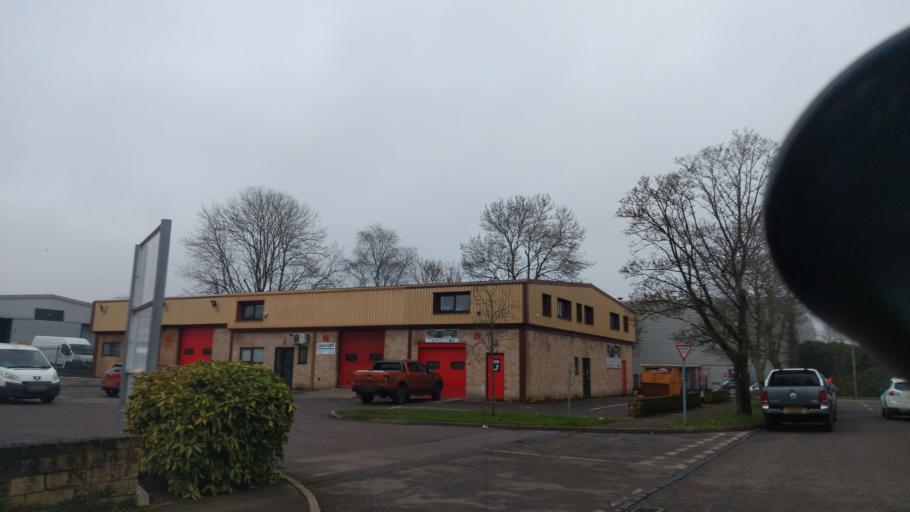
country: GB
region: England
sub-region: Wiltshire
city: Melksham
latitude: 51.3586
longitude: -2.1299
